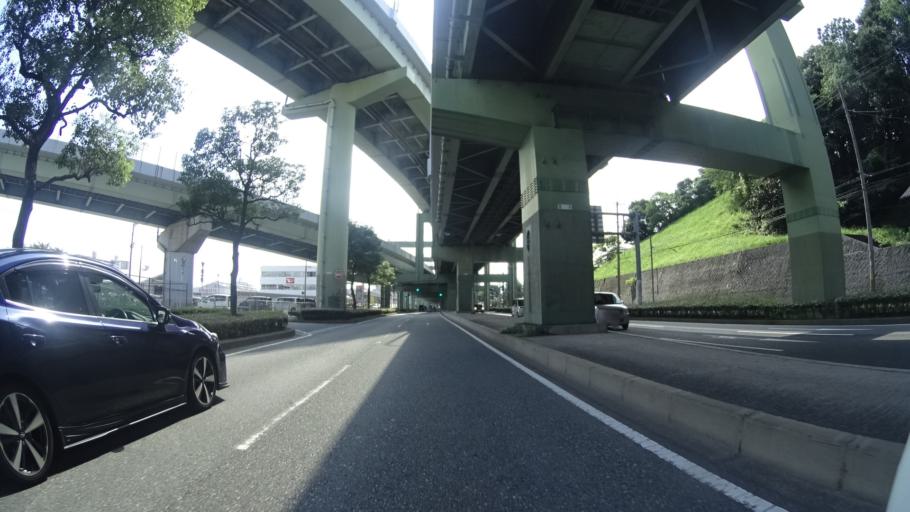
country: JP
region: Fukuoka
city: Kitakyushu
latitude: 33.8844
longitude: 130.8632
